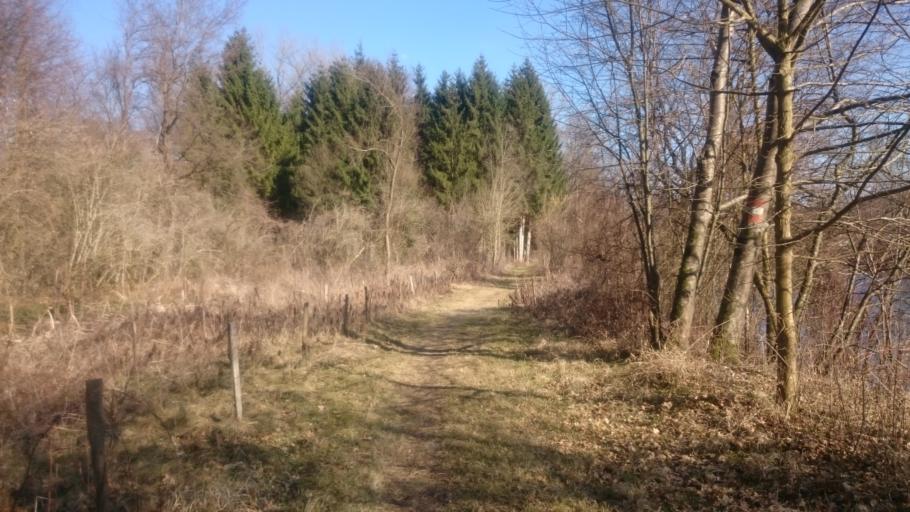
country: SI
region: Sentilj
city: Selnica ob Muri
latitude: 46.7072
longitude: 15.6759
